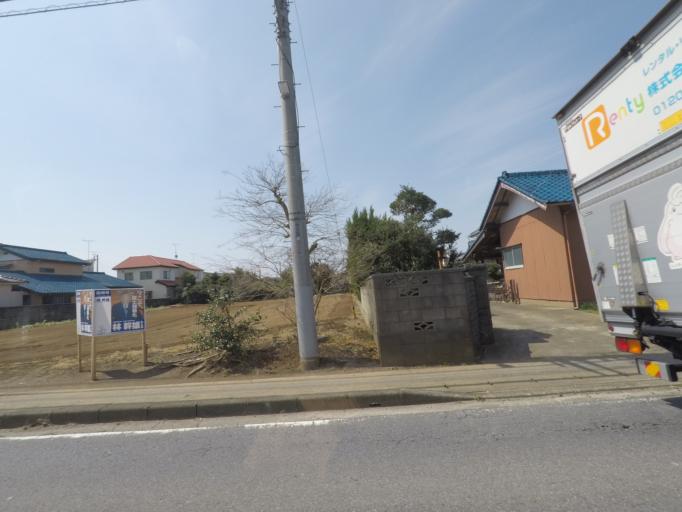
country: JP
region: Chiba
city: Narita
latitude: 35.7523
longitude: 140.3720
